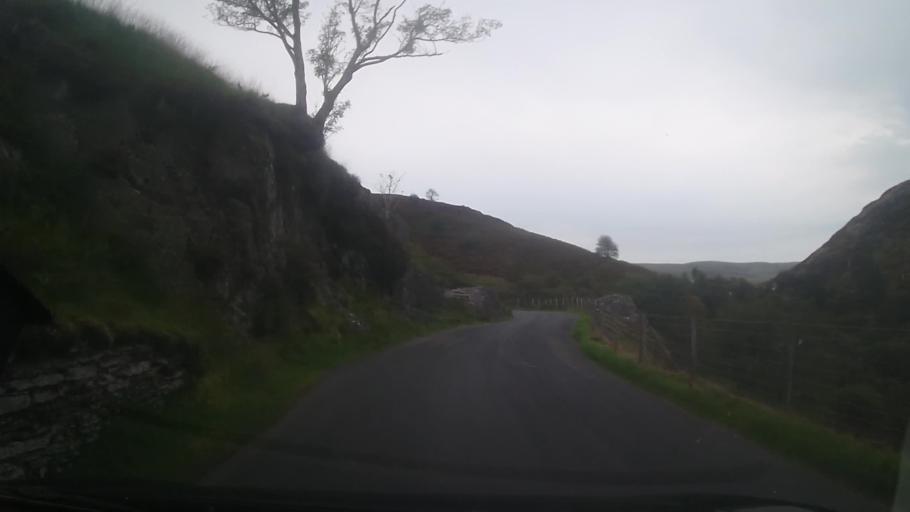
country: GB
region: Wales
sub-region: Sir Powys
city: Rhayader
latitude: 52.3011
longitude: -3.6233
